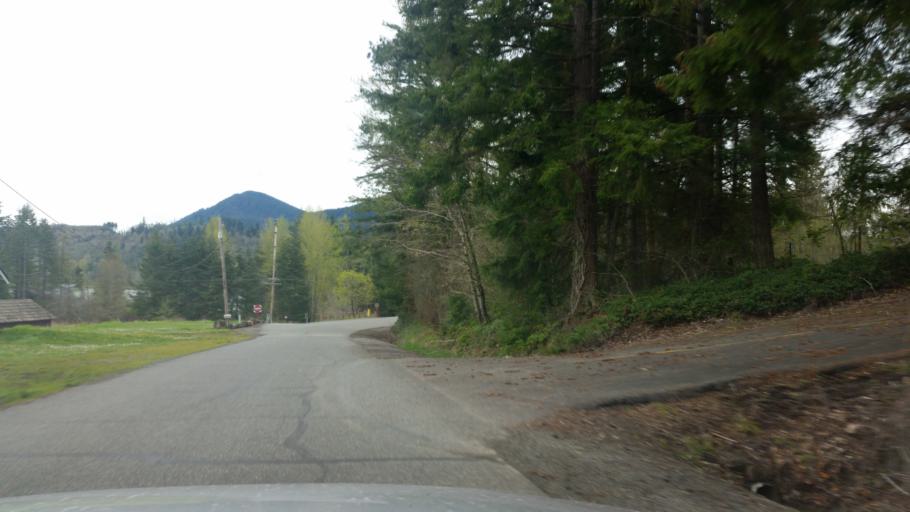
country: US
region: Washington
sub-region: Pierce County
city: Eatonville
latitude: 46.8006
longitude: -122.2918
